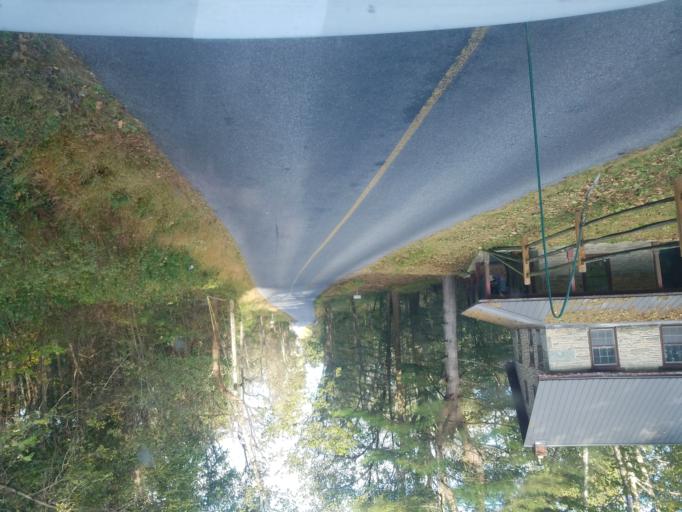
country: US
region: Pennsylvania
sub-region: Adams County
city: Biglerville
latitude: 39.8835
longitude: -77.3296
